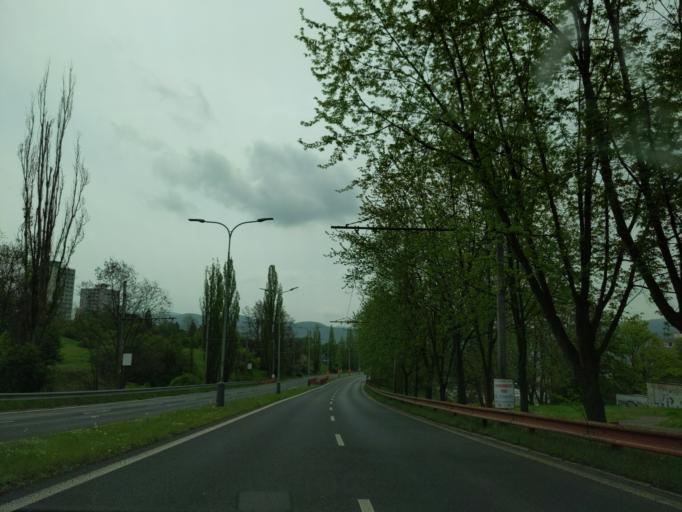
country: CZ
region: Ustecky
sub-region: Okres Usti nad Labem
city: Usti nad Labem
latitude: 50.6747
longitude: 14.0318
